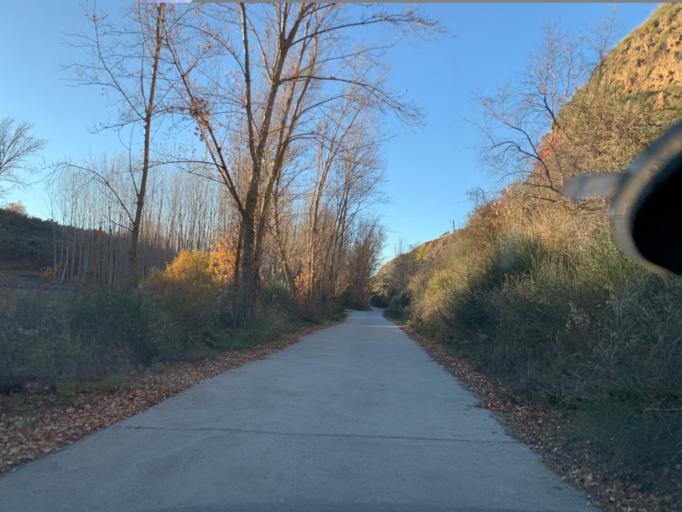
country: ES
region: Andalusia
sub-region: Provincia de Granada
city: Dilar
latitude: 37.0649
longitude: -3.5669
